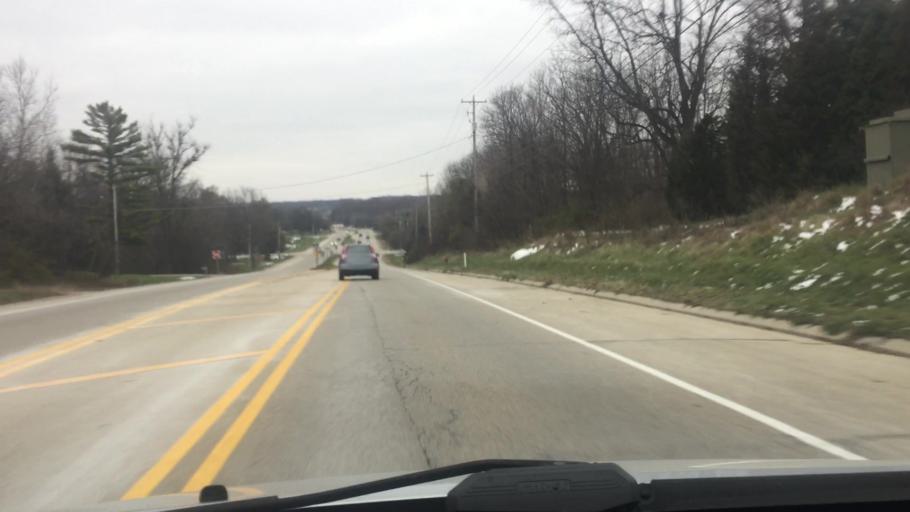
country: US
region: Wisconsin
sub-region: Waukesha County
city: Delafield
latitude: 43.0670
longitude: -88.3668
